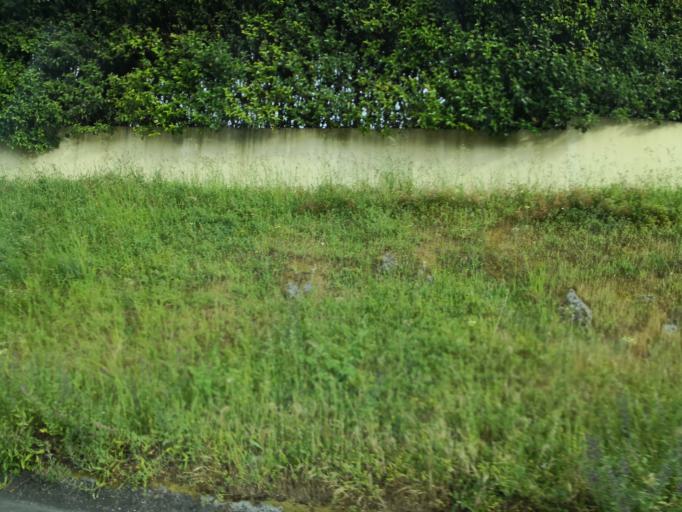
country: PT
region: Porto
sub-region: Gondomar
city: Rio Tinto
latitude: 41.1690
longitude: -8.5730
